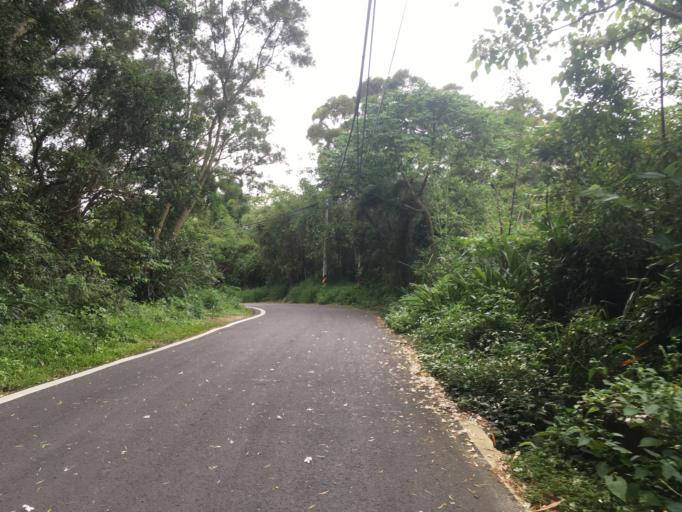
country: TW
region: Taiwan
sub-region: Hsinchu
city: Hsinchu
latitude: 24.7447
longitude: 120.9840
